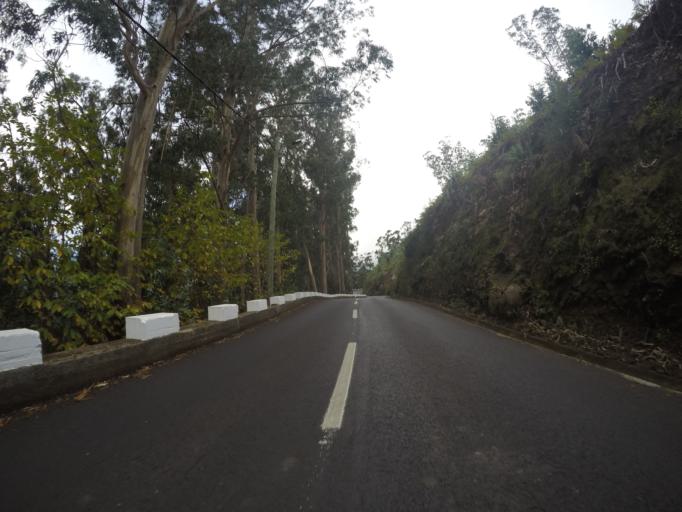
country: PT
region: Madeira
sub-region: Camara de Lobos
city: Curral das Freiras
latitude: 32.6911
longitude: -16.9557
